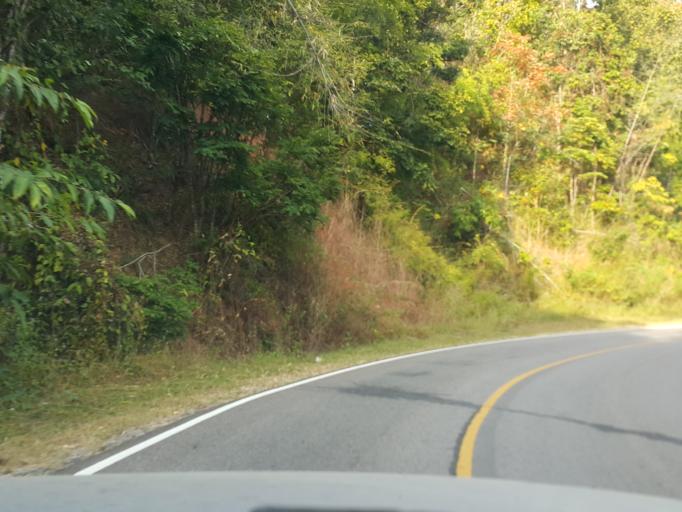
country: TH
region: Chiang Mai
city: Mae On
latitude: 18.7236
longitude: 99.2697
